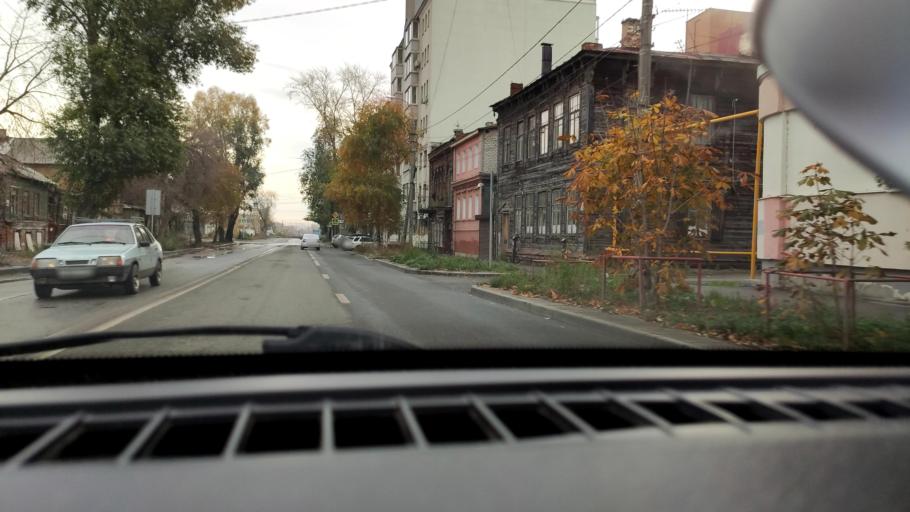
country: RU
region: Samara
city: Samara
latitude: 53.1821
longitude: 50.1011
